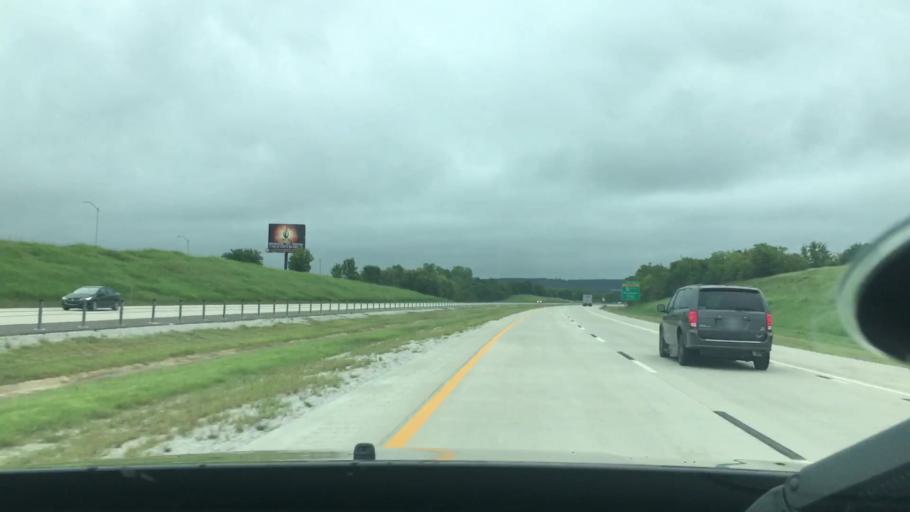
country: US
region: Oklahoma
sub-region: Okmulgee County
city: Henryetta
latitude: 35.4339
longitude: -96.0105
